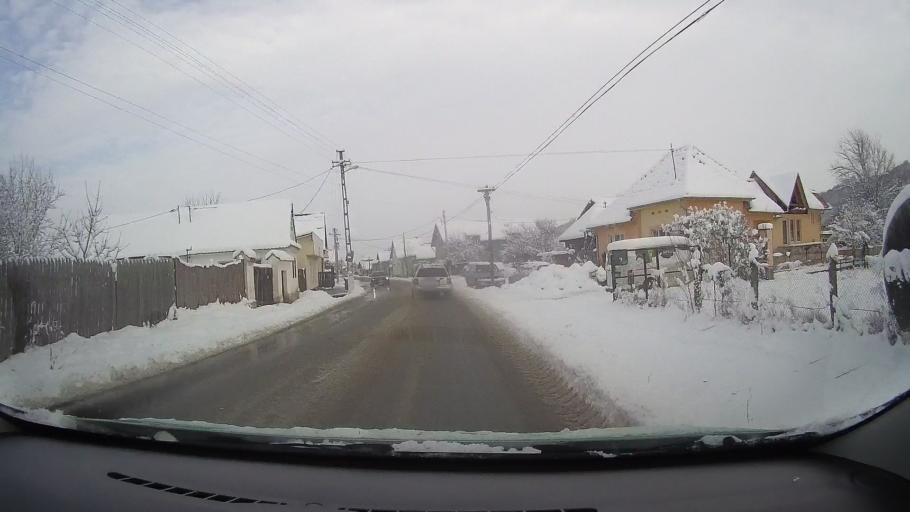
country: RO
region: Alba
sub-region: Comuna Pianu
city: Pianu de Jos
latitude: 45.9286
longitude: 23.4860
